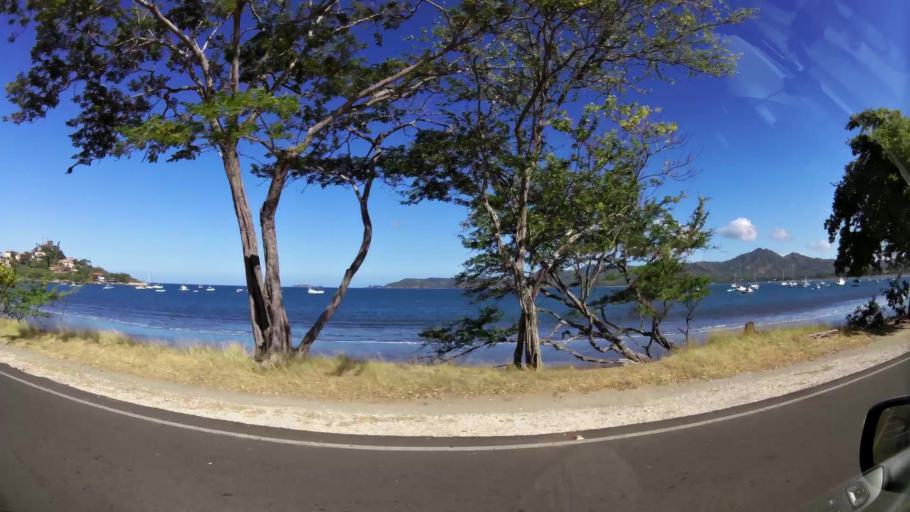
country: CR
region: Guanacaste
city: Sardinal
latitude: 10.4369
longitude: -85.7823
